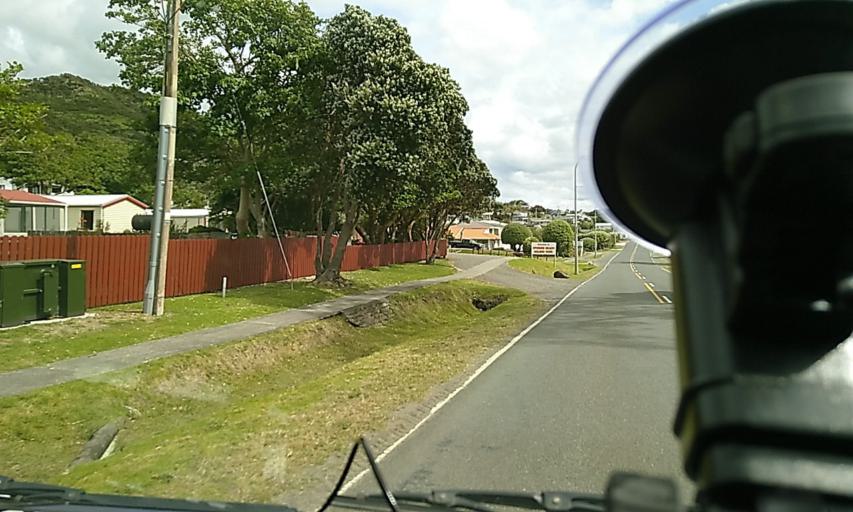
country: NZ
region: Northland
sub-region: Far North District
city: Ahipara
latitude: -35.5082
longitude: 173.3901
